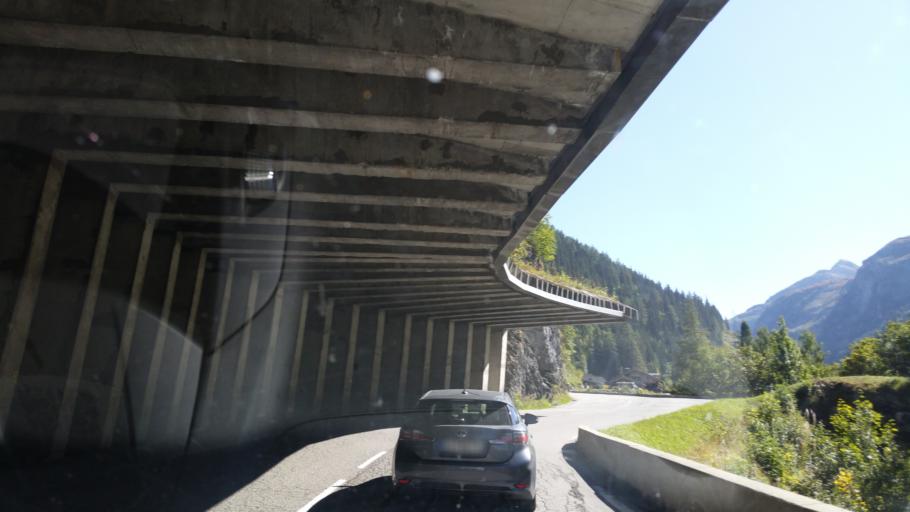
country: FR
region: Rhone-Alpes
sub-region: Departement de la Savoie
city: Tignes
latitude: 45.5354
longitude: 6.9145
